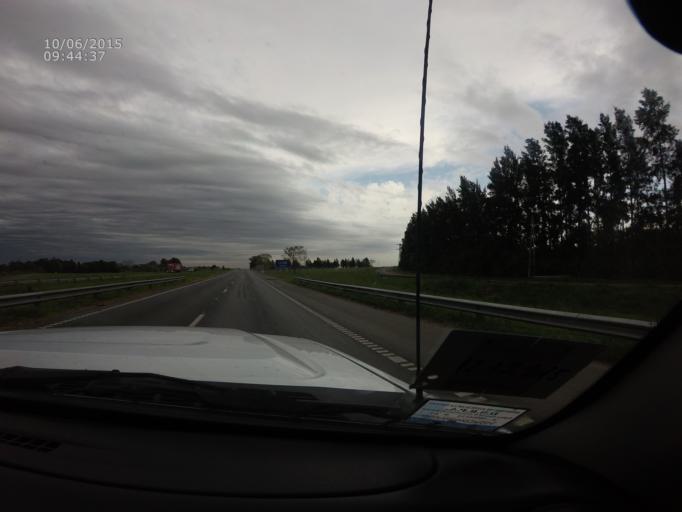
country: AR
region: Buenos Aires
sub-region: Partido de Zarate
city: Zarate
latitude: -34.0619
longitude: -59.2760
